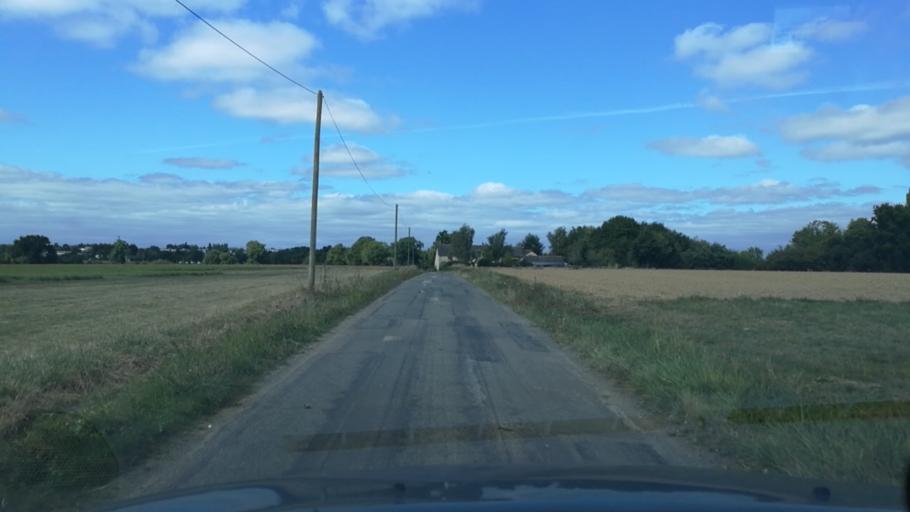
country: FR
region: Brittany
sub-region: Departement d'Ille-et-Vilaine
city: Montgermont
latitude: 48.1442
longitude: -1.7090
